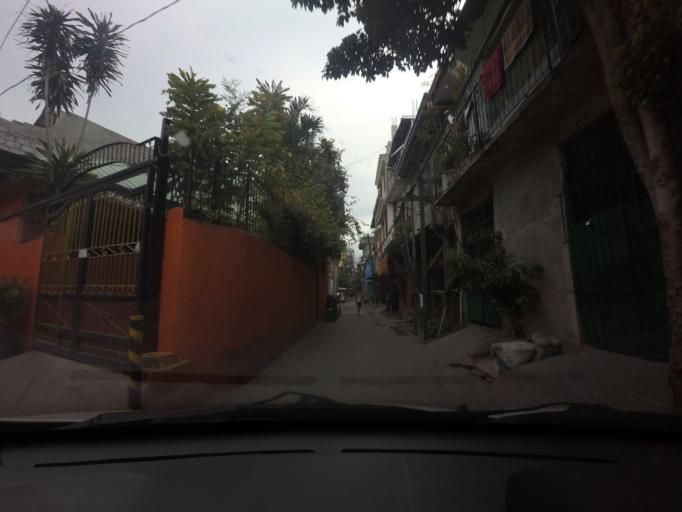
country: PH
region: Calabarzon
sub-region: Province of Rizal
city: Pateros
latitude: 14.5251
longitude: 121.0600
